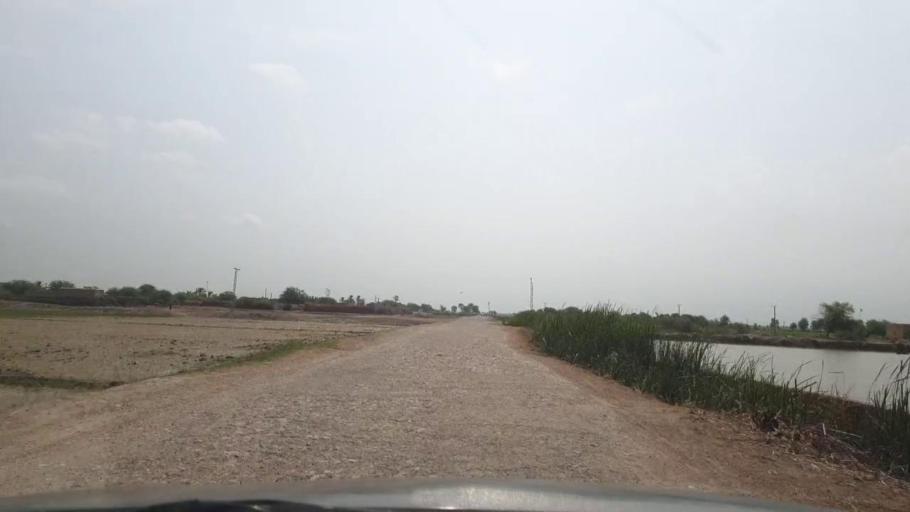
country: PK
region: Sindh
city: Ratodero
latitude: 27.8417
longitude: 68.3198
